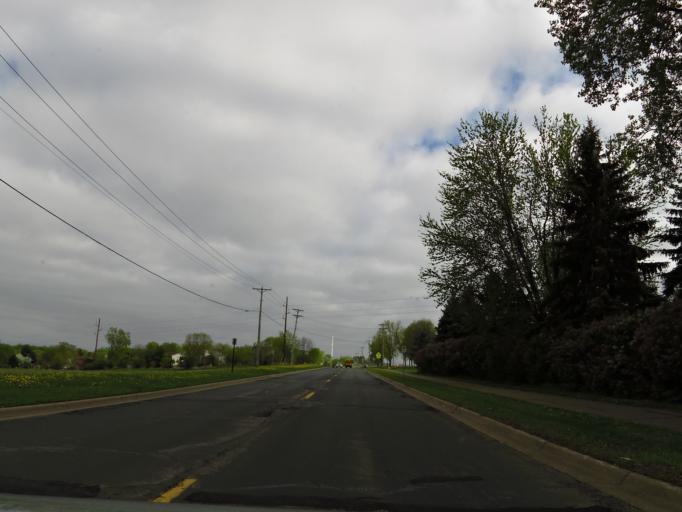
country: US
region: Minnesota
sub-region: Washington County
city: Woodbury
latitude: 44.9352
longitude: -92.9755
